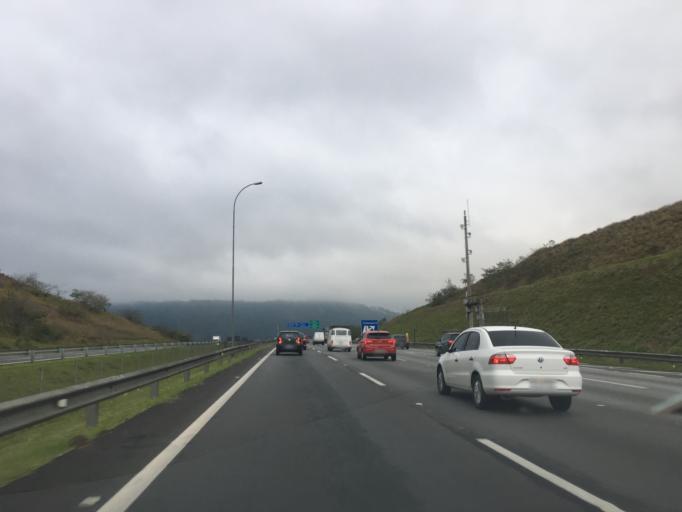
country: BR
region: Sao Paulo
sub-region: Caieiras
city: Caieiras
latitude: -23.4421
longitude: -46.7740
